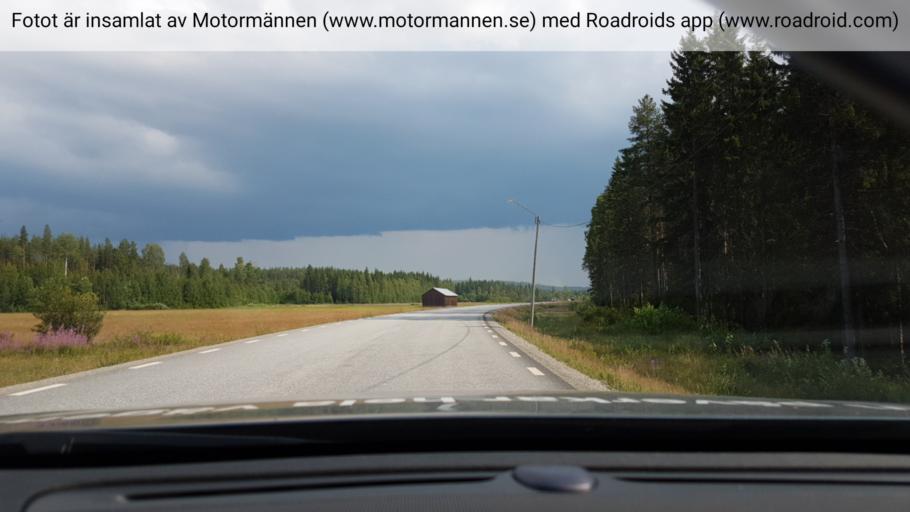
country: SE
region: Vaesterbotten
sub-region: Vindelns Kommun
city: Vindeln
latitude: 64.2012
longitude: 19.4475
